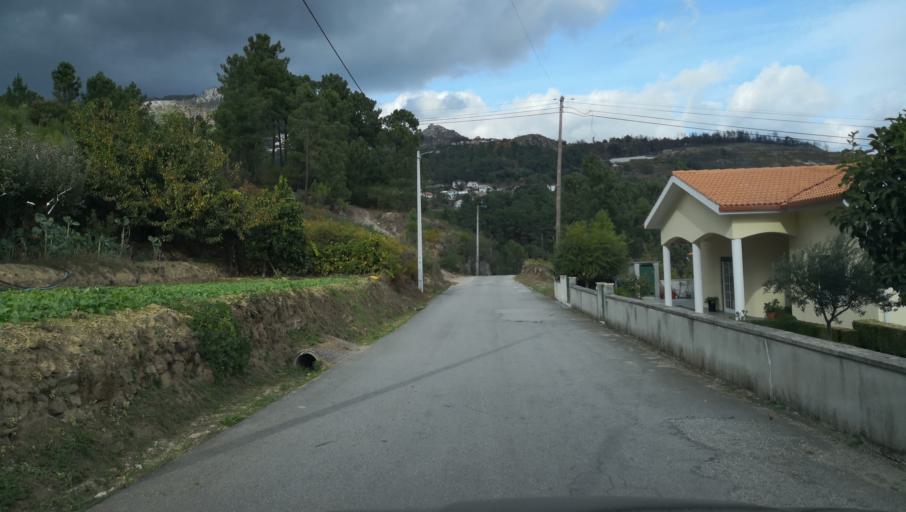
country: PT
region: Vila Real
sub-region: Vila Real
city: Vila Real
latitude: 41.3210
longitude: -7.7723
